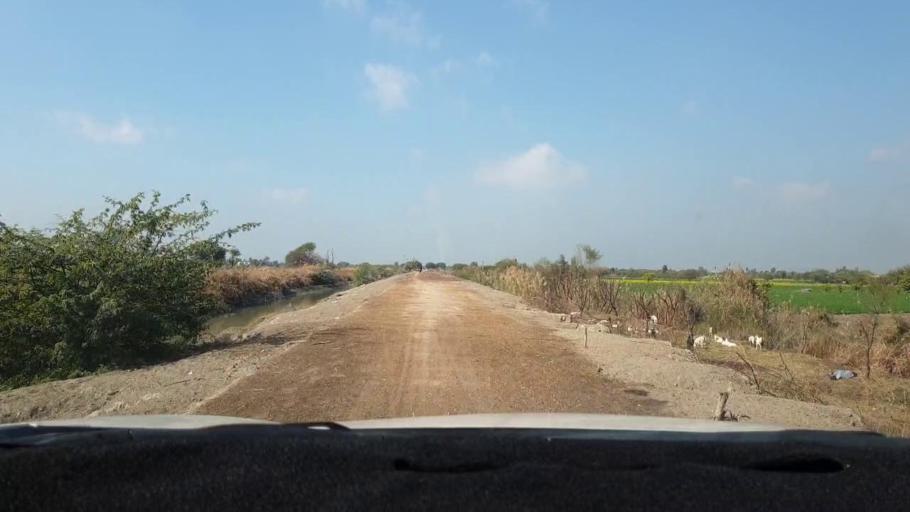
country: PK
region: Sindh
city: Berani
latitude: 25.7421
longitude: 68.9232
